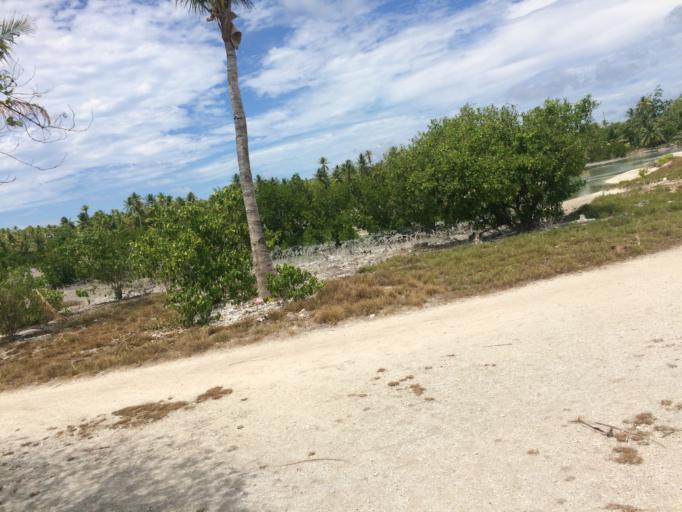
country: KI
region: Gilbert Islands
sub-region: Marakei
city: Rawannawi Village
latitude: 1.9151
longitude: 172.9459
